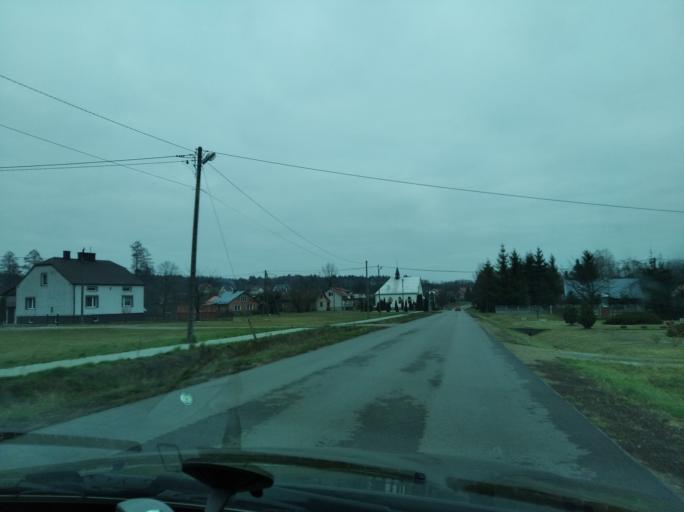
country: PL
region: Subcarpathian Voivodeship
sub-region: Powiat lancucki
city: Rakszawa
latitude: 50.1636
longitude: 22.1948
